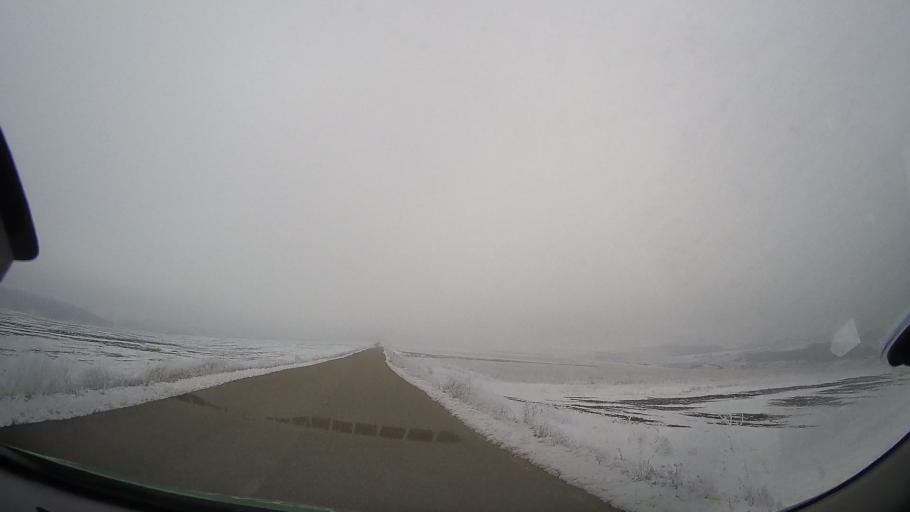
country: RO
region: Vaslui
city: Coroiesti
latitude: 46.2298
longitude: 27.4780
